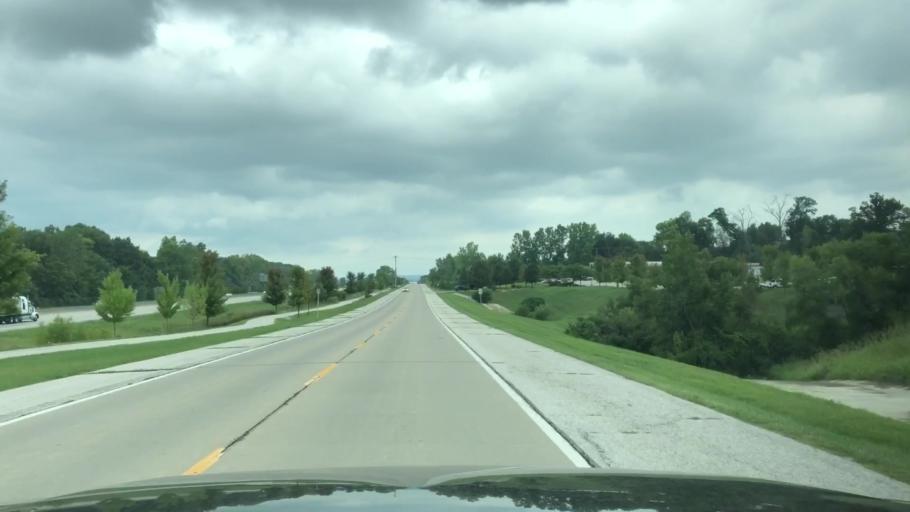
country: US
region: Missouri
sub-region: Saint Charles County
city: Saint Charles
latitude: 38.8117
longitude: -90.4873
